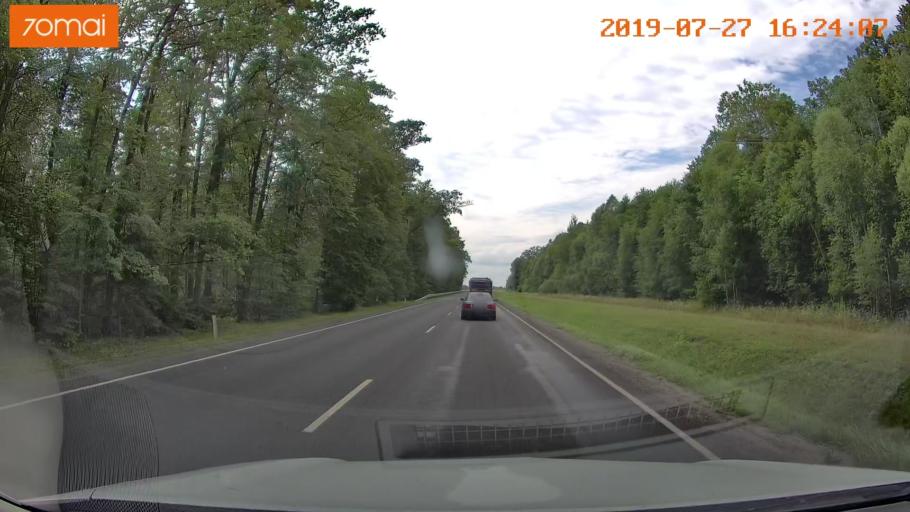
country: RU
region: Kaliningrad
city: Zheleznodorozhnyy
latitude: 54.6331
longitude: 21.4592
